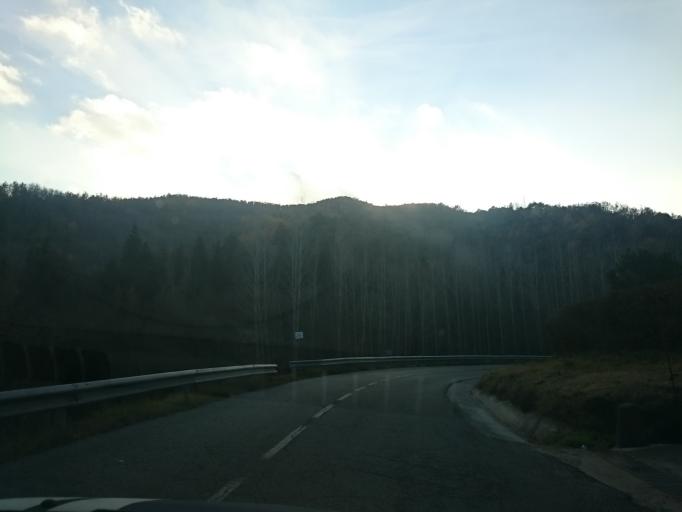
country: ES
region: Catalonia
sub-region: Provincia de Girona
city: Viladrau
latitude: 41.8508
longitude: 2.3695
